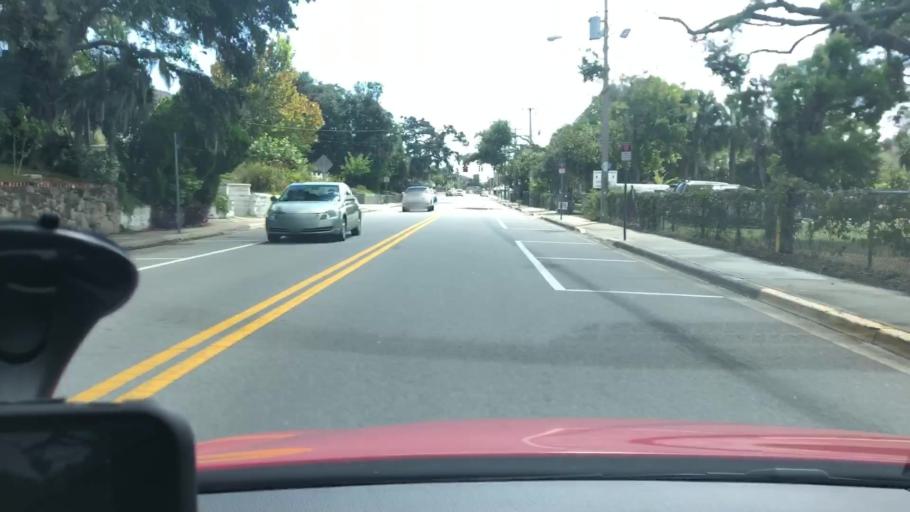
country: US
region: Florida
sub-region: Volusia County
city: Daytona Beach
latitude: 29.2279
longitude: -81.0143
